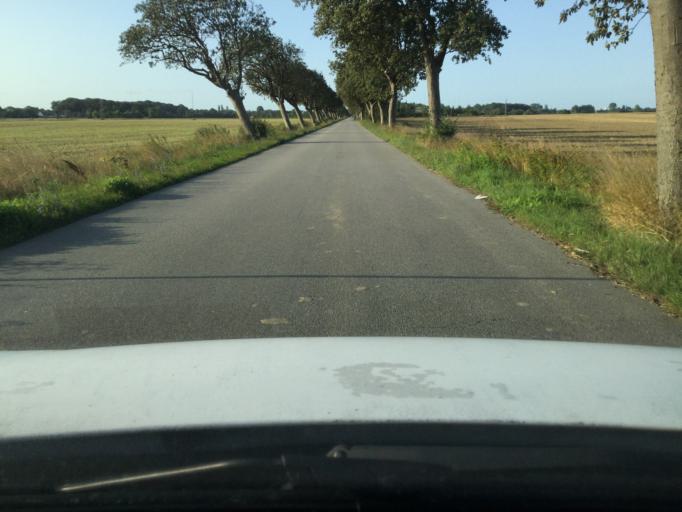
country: DK
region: Zealand
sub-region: Lolland Kommune
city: Rodby
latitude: 54.7076
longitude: 11.3886
